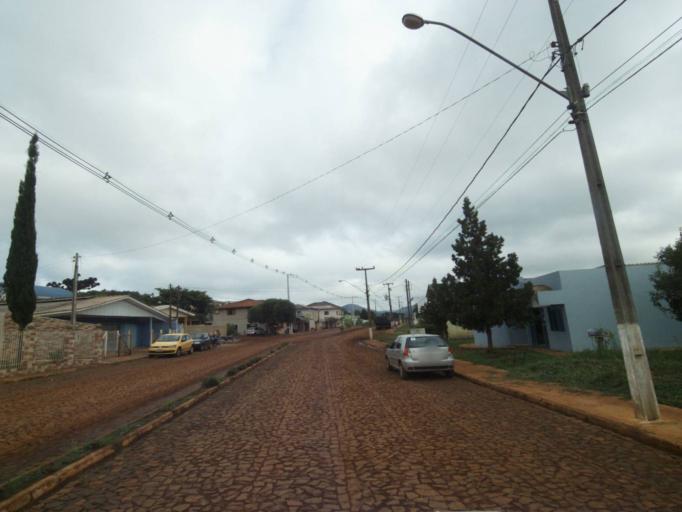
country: BR
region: Parana
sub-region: Pitanga
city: Pitanga
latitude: -24.9397
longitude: -51.8687
